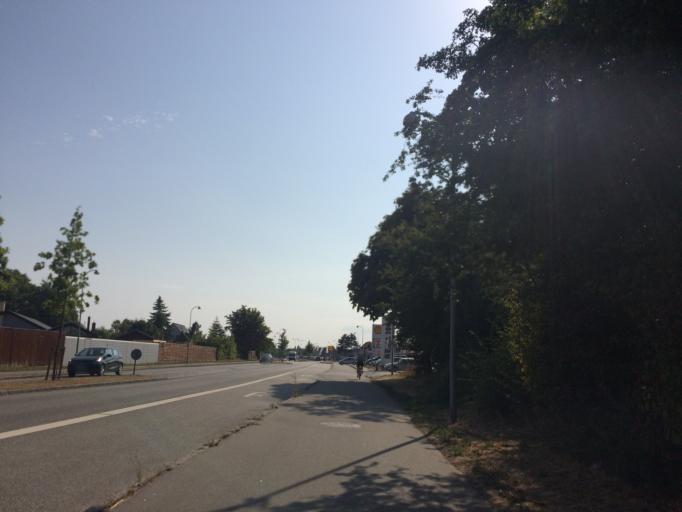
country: DK
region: Capital Region
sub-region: Ishoj Kommune
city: Ishoj
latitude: 55.6096
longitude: 12.3600
